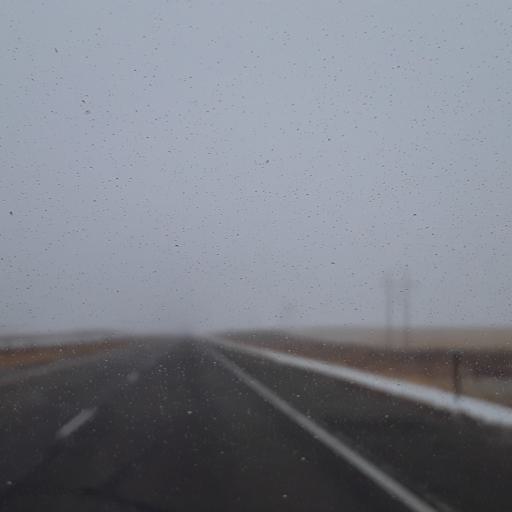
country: US
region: Colorado
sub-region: Logan County
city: Sterling
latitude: 40.7874
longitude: -102.8983
